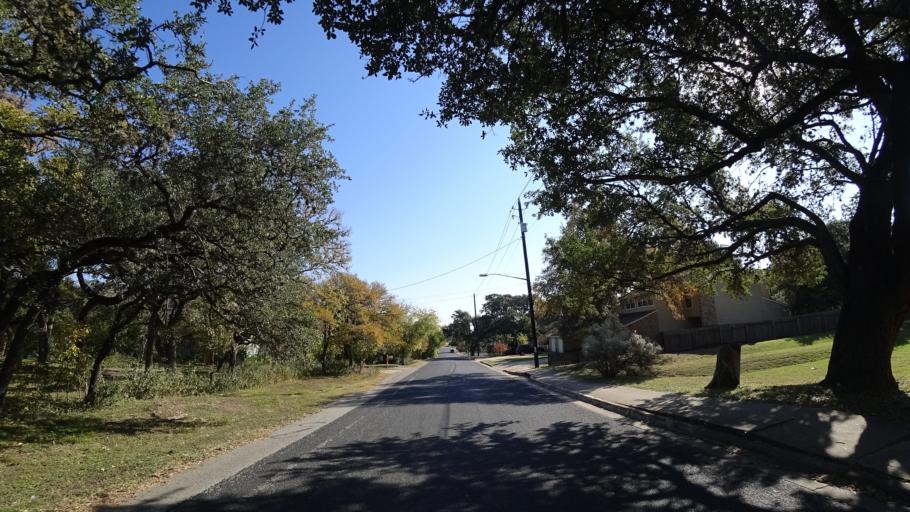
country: US
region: Texas
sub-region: Travis County
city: Barton Creek
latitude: 30.2341
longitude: -97.8499
